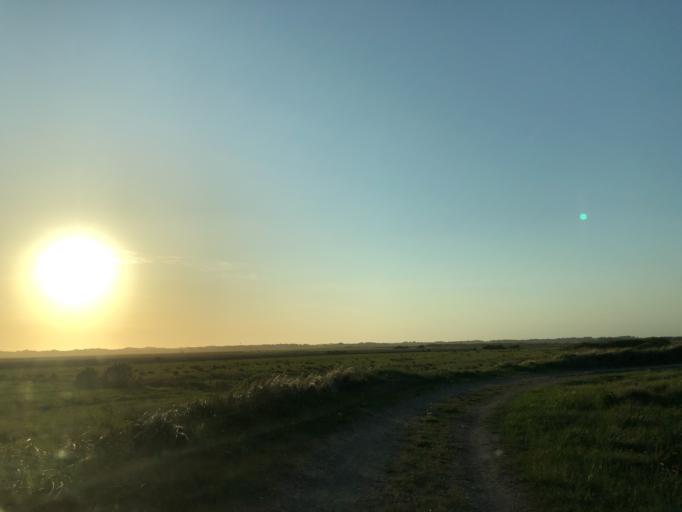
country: DK
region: Central Jutland
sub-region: Holstebro Kommune
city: Ulfborg
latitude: 56.2419
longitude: 8.1623
